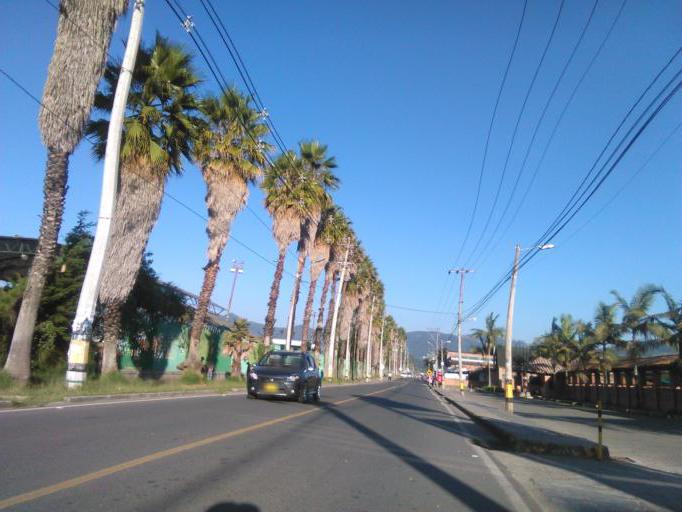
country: CO
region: Antioquia
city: La Ceja
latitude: 6.0289
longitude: -75.4271
